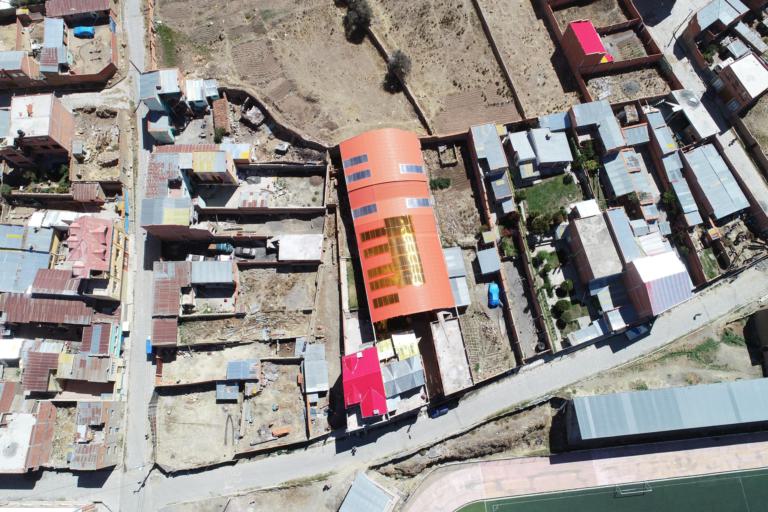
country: BO
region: La Paz
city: Achacachi
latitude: -16.0440
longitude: -68.6824
